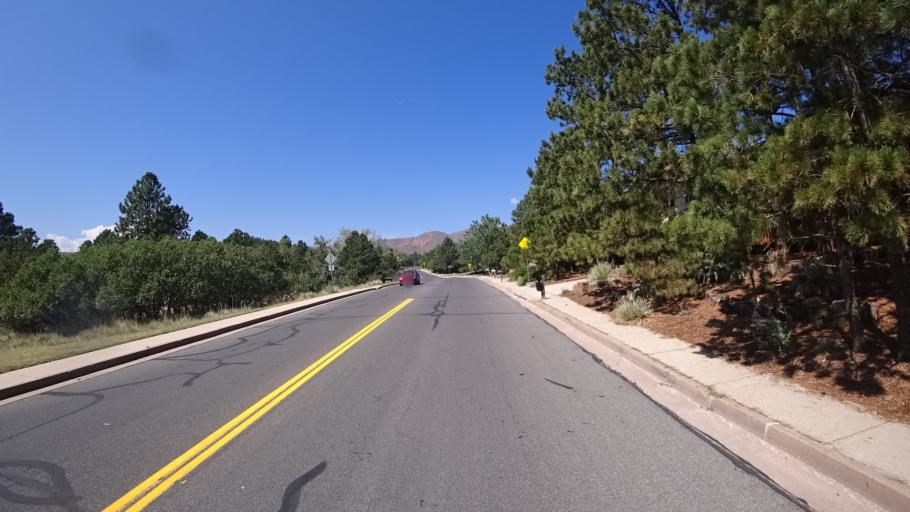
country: US
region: Colorado
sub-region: El Paso County
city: Air Force Academy
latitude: 38.9299
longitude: -104.8478
